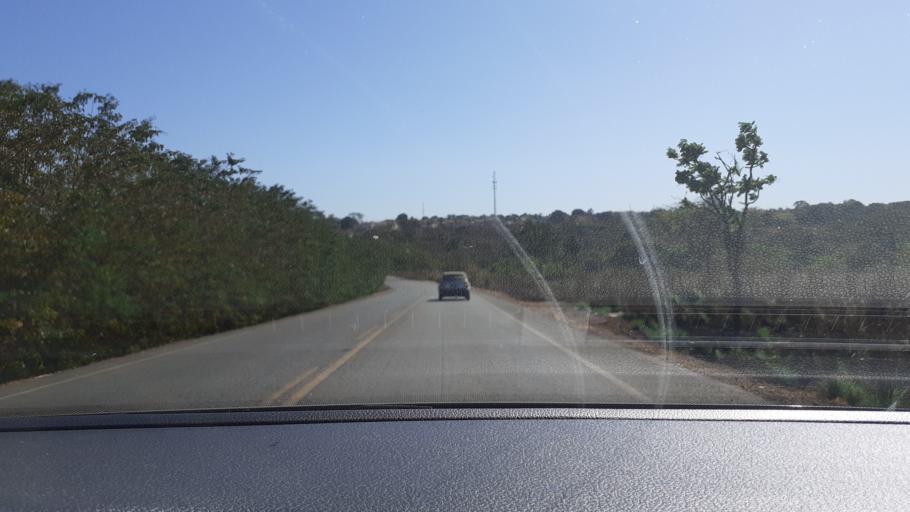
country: BR
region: Goias
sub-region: Aparecida De Goiania
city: Aparecida de Goiania
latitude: -16.8504
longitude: -49.2537
